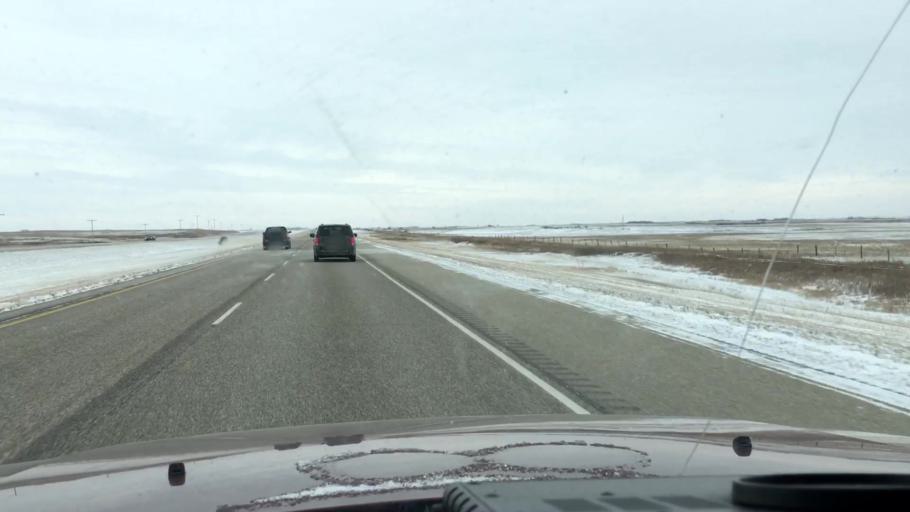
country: CA
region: Saskatchewan
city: Saskatoon
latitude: 51.5963
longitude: -106.3900
